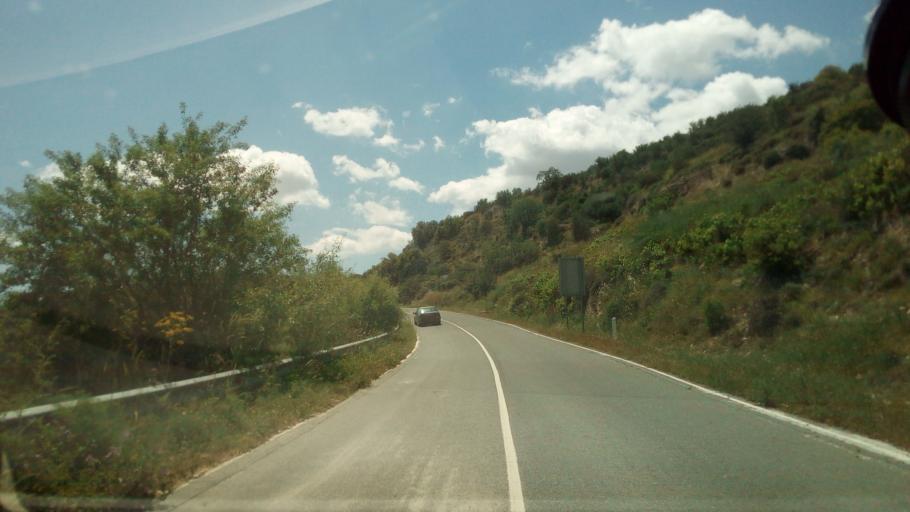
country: CY
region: Limassol
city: Pachna
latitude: 34.8151
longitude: 32.7783
